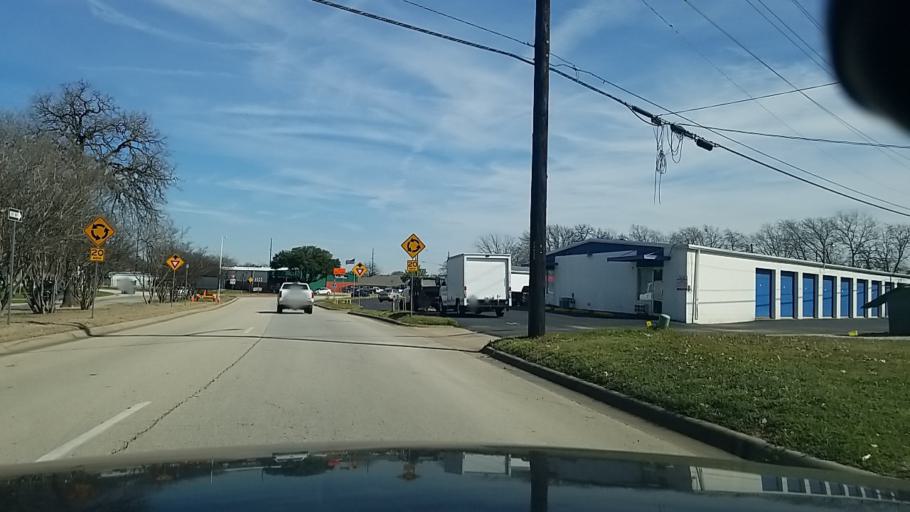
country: US
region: Texas
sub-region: Denton County
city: Denton
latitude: 33.1992
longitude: -97.1221
